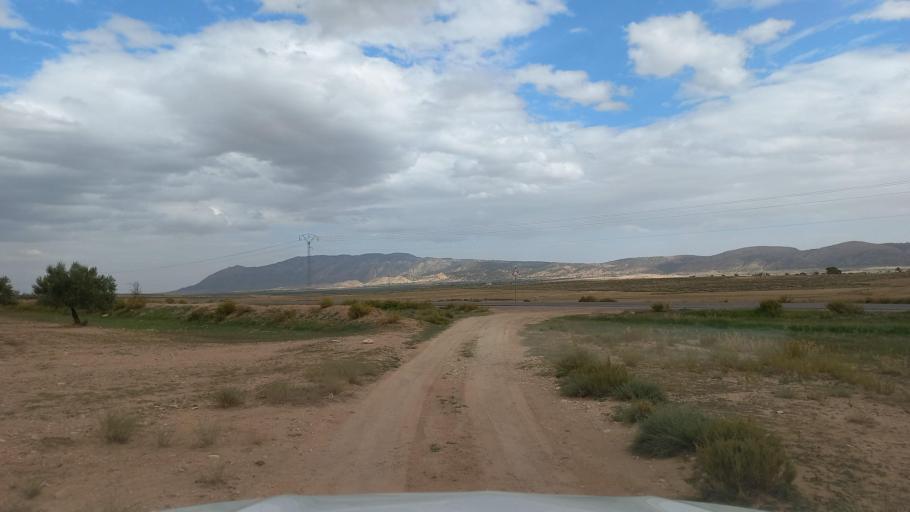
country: TN
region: Al Qasrayn
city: Sbiba
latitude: 35.3837
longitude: 9.1109
